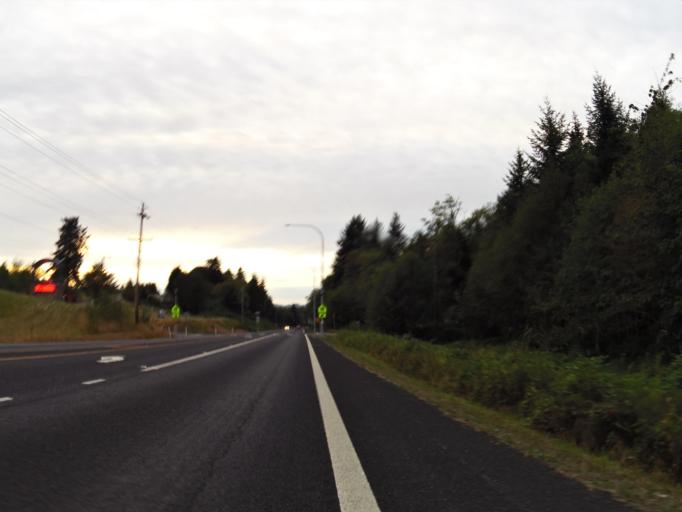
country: US
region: Washington
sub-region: Wahkiakum County
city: Cathlamet
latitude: 46.2016
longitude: -123.3759
